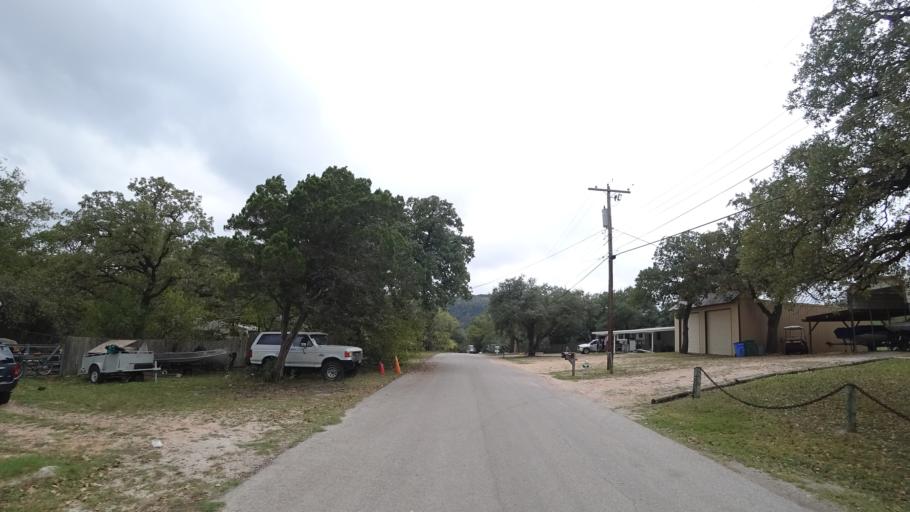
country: US
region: Texas
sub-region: Travis County
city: Bee Cave
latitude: 30.3329
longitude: -97.9280
